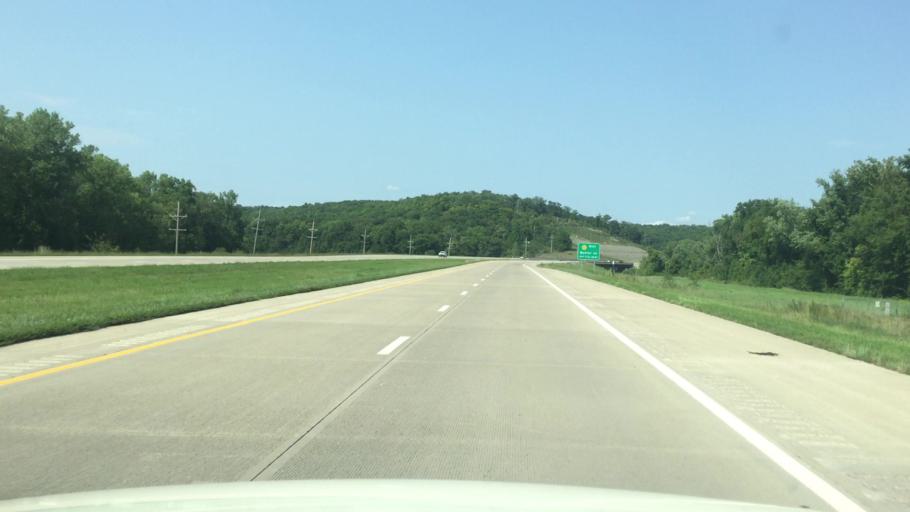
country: US
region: Kansas
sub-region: Linn County
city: Pleasanton
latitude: 38.2446
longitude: -94.6882
